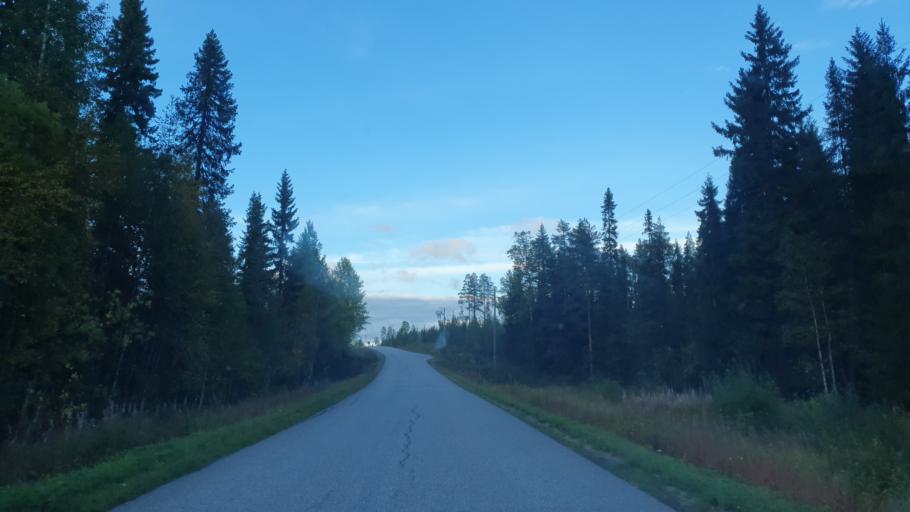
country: FI
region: Kainuu
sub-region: Kehys-Kainuu
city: Kuhmo
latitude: 64.4164
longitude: 29.9569
